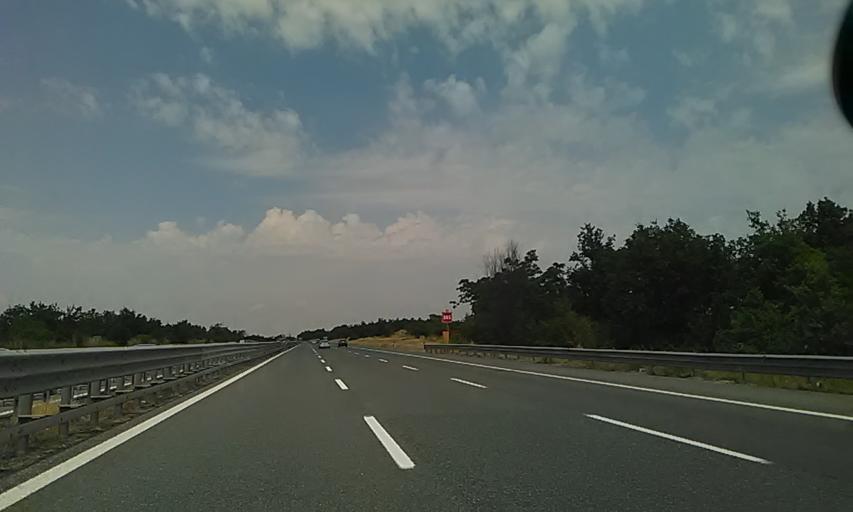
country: IT
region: Piedmont
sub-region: Provincia di Alessandria
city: Predosa
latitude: 44.7271
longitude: 8.6655
